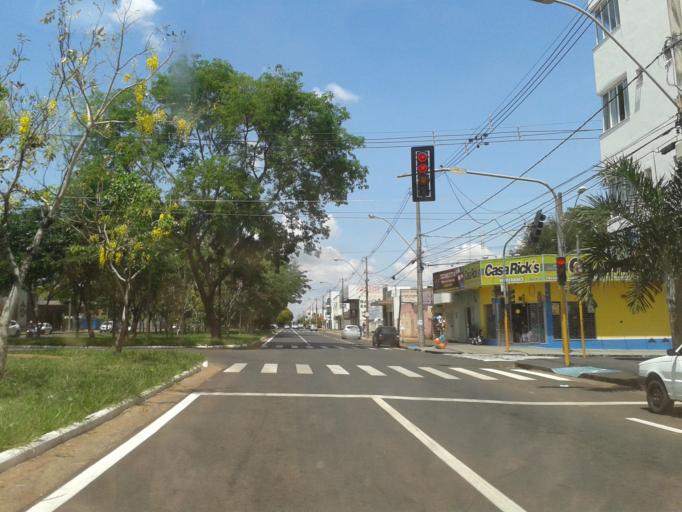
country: BR
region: Minas Gerais
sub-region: Araguari
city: Araguari
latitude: -18.6568
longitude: -48.1903
